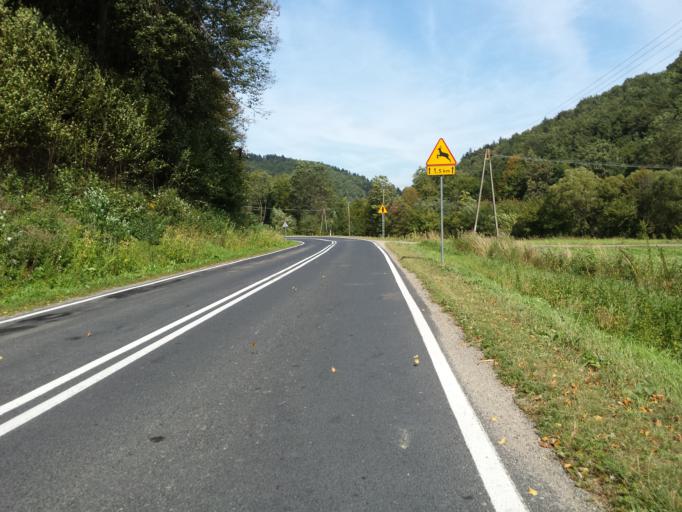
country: PL
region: Subcarpathian Voivodeship
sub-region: Powiat leski
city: Baligrod
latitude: 49.3623
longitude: 22.2761
